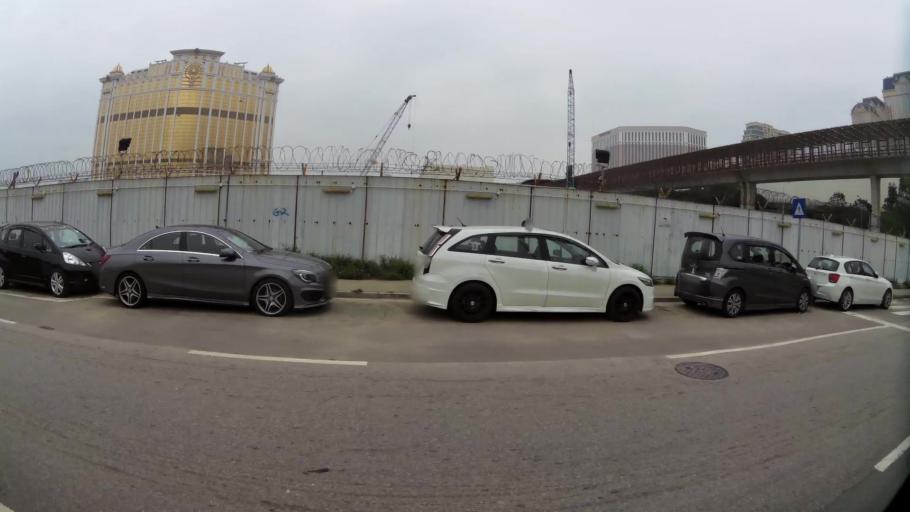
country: MO
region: Macau
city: Macau
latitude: 22.1430
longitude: 113.5570
